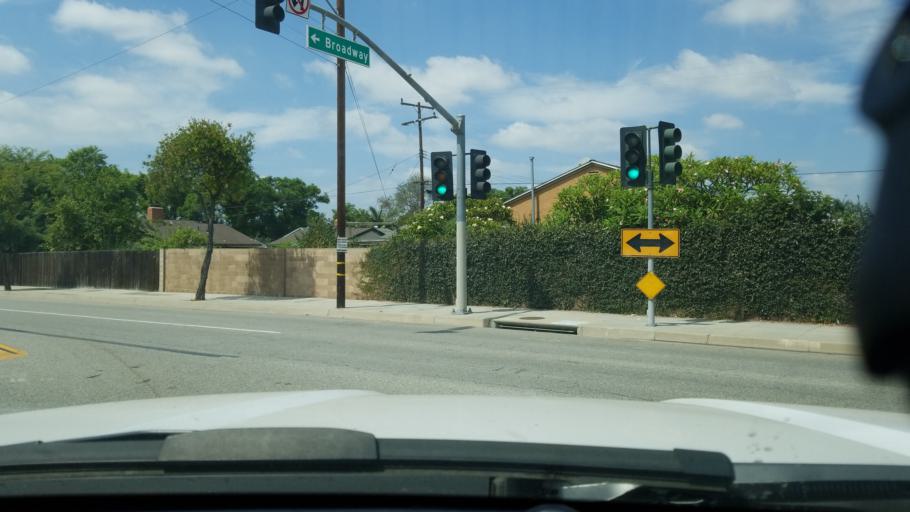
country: US
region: California
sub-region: Los Angeles County
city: South Whittier
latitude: 33.9417
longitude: -118.0301
